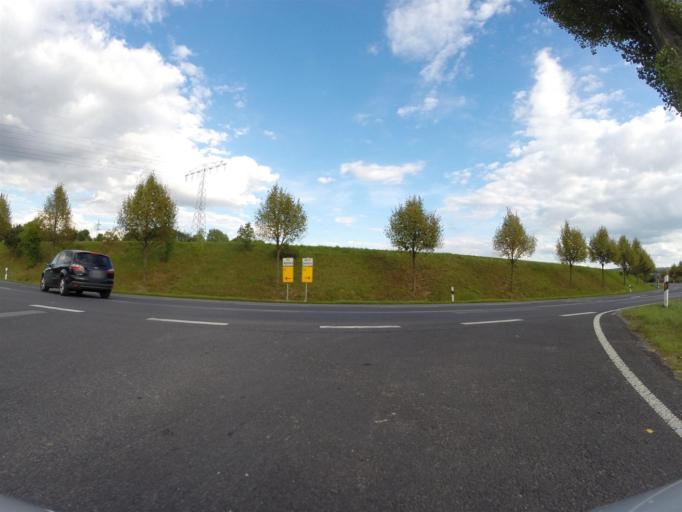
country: DE
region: Thuringia
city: Mellingen
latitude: 50.9465
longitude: 11.3963
